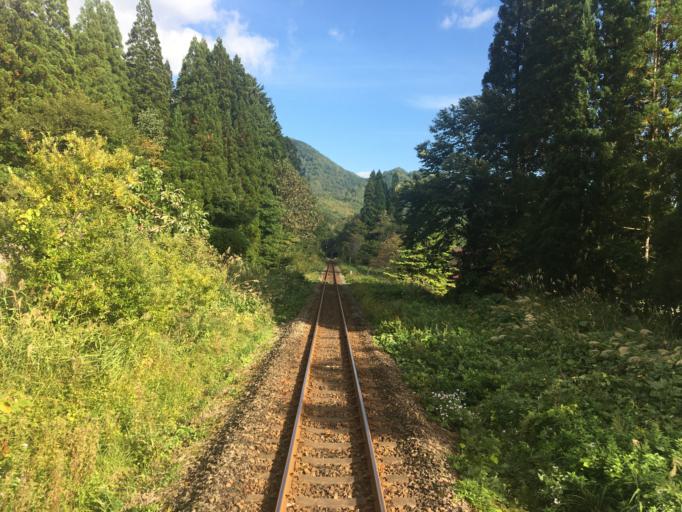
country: JP
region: Akita
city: Kakunodatemachi
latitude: 39.8657
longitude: 140.5718
